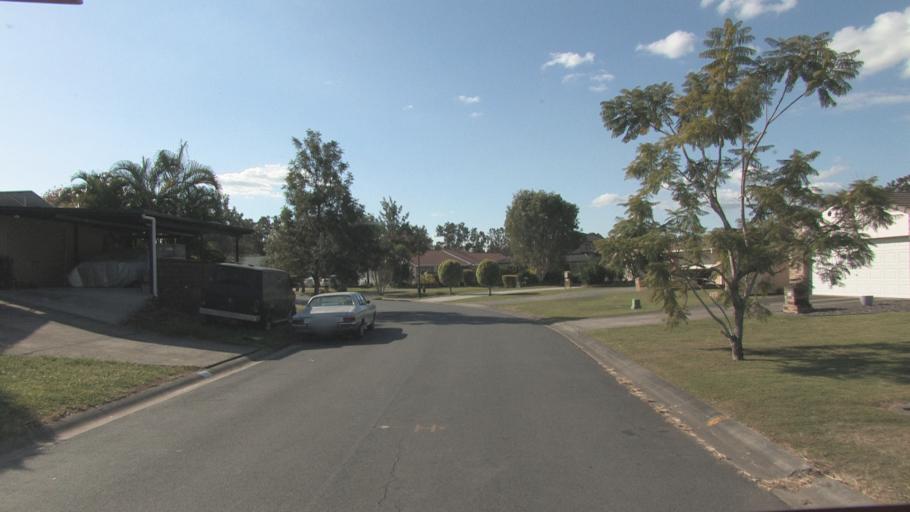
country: AU
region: Queensland
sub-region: Logan
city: Windaroo
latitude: -27.7520
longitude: 153.1954
